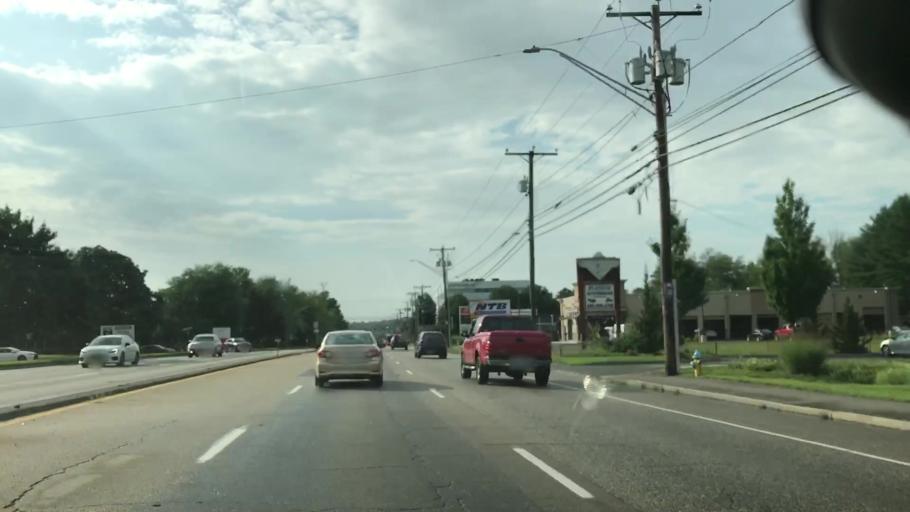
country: US
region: New Hampshire
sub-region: Hillsborough County
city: Nashua
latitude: 42.7955
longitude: -71.5276
